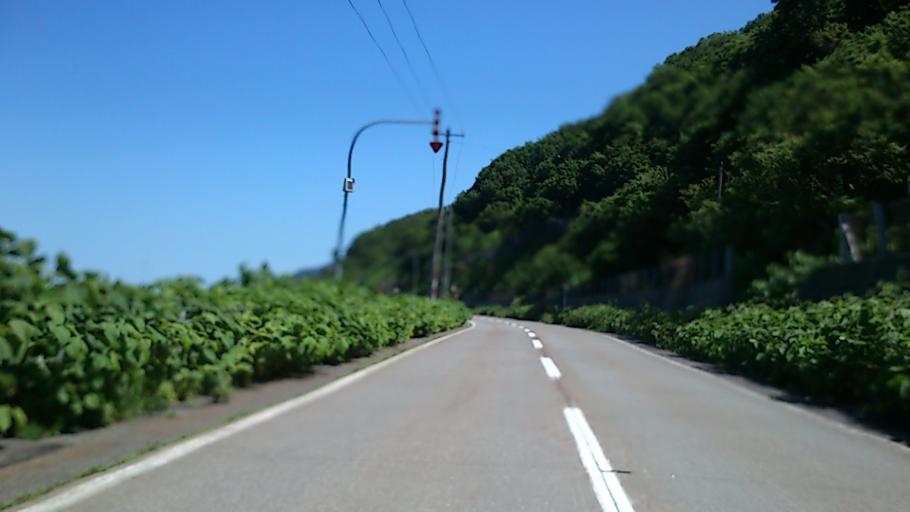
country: JP
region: Hokkaido
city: Rumoi
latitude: 43.7432
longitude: 141.3439
